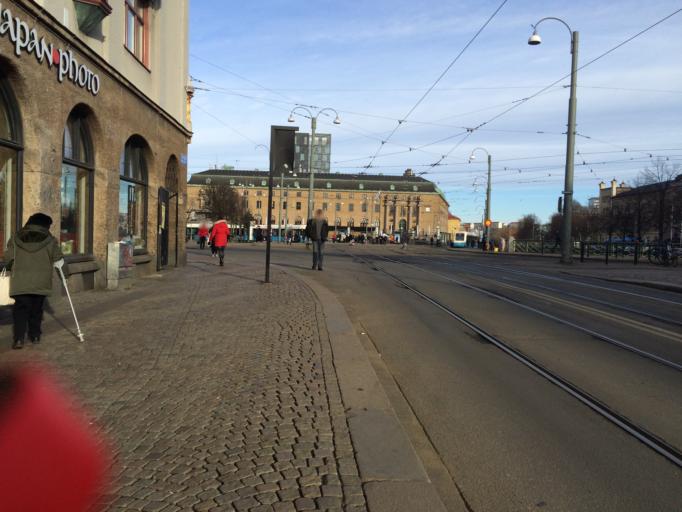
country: SE
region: Vaestra Goetaland
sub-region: Goteborg
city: Goeteborg
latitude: 57.7074
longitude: 11.9715
